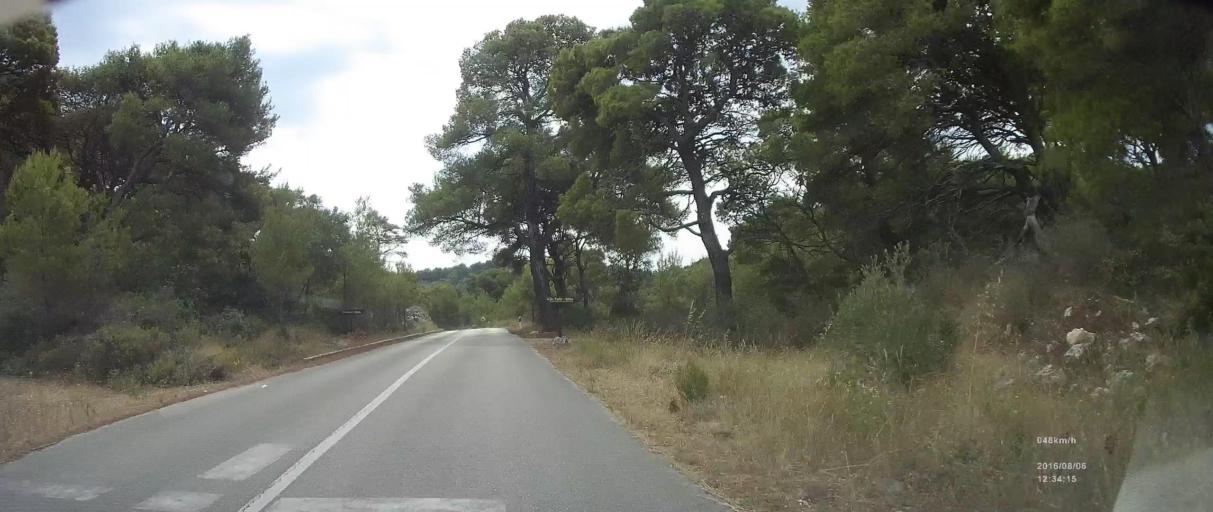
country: HR
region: Dubrovacko-Neretvanska
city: Ston
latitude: 42.7098
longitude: 17.7287
